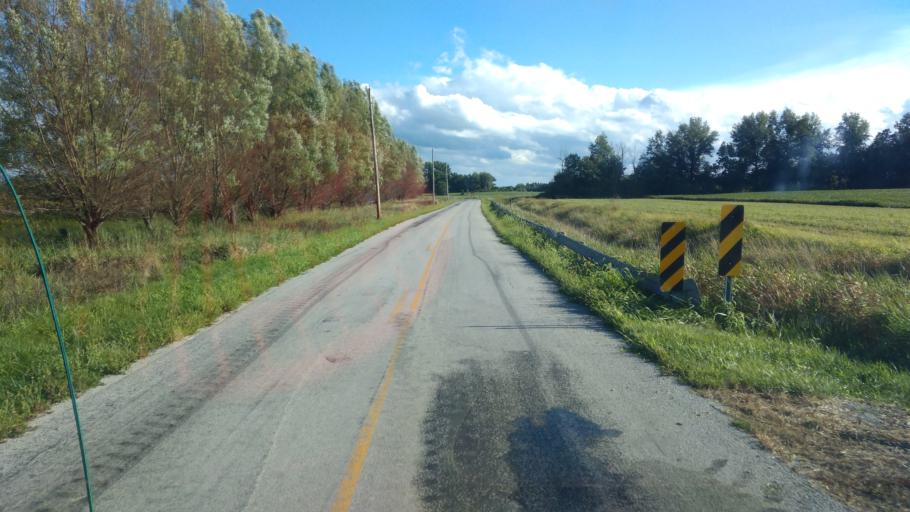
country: US
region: Ohio
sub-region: Hardin County
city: Forest
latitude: 40.7550
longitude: -83.6048
